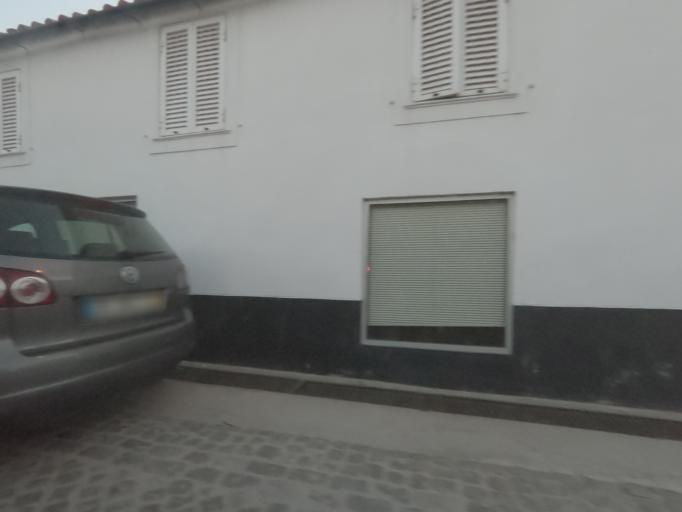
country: PT
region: Vila Real
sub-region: Peso da Regua
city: Peso da Regua
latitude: 41.1783
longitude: -7.7266
